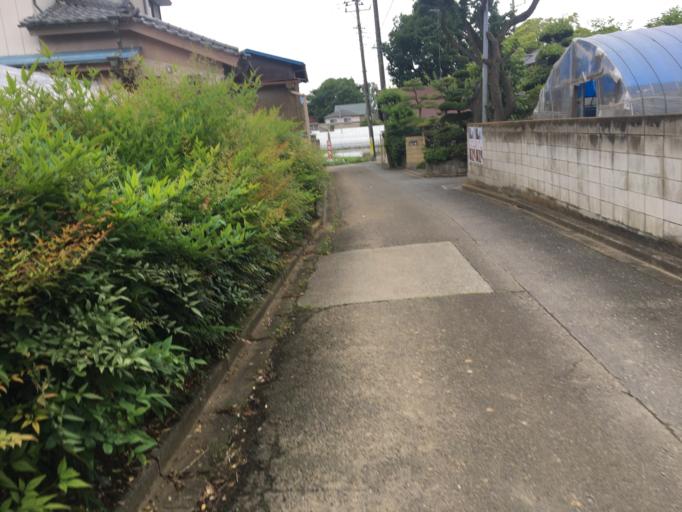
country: JP
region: Saitama
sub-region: Kawaguchi-shi
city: Hatogaya-honcho
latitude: 35.8638
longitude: 139.7175
